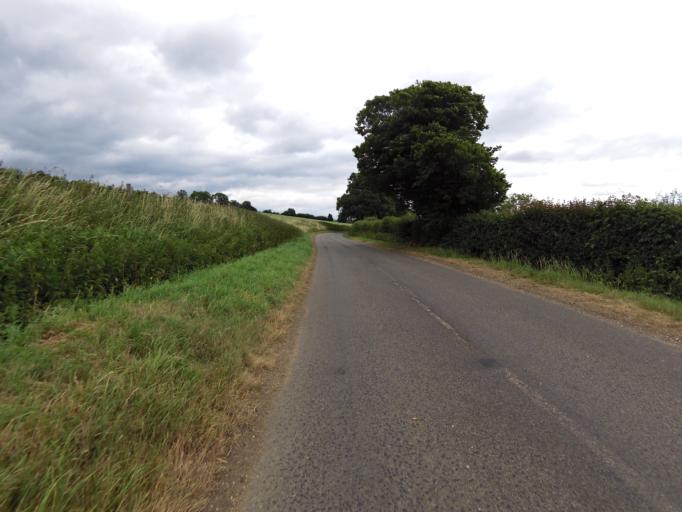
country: GB
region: England
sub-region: Norfolk
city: Harleston
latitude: 52.4287
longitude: 1.3613
